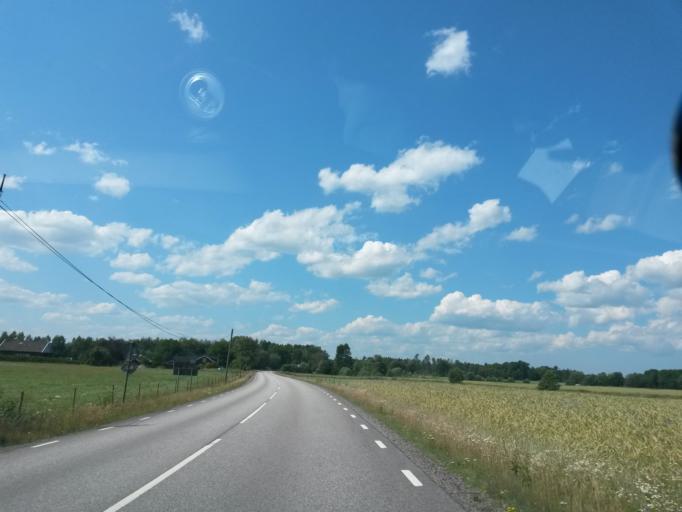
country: SE
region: Vaestra Goetaland
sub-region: Essunga Kommun
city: Nossebro
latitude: 58.1570
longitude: 12.8282
